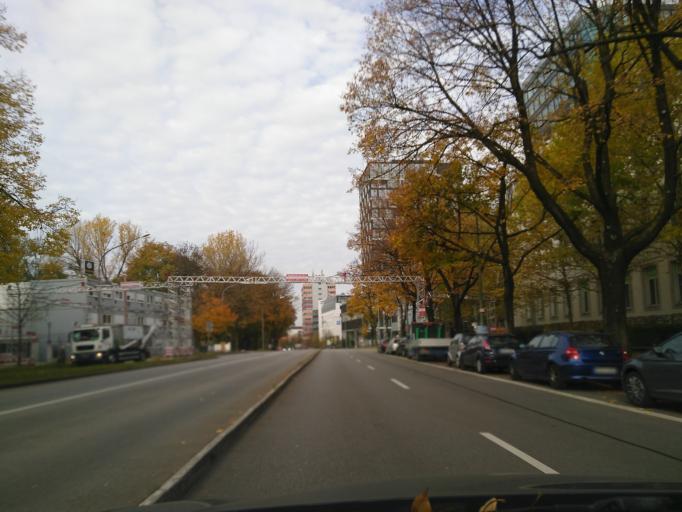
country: DE
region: Bavaria
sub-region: Upper Bavaria
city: Bogenhausen
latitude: 48.1220
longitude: 11.6048
